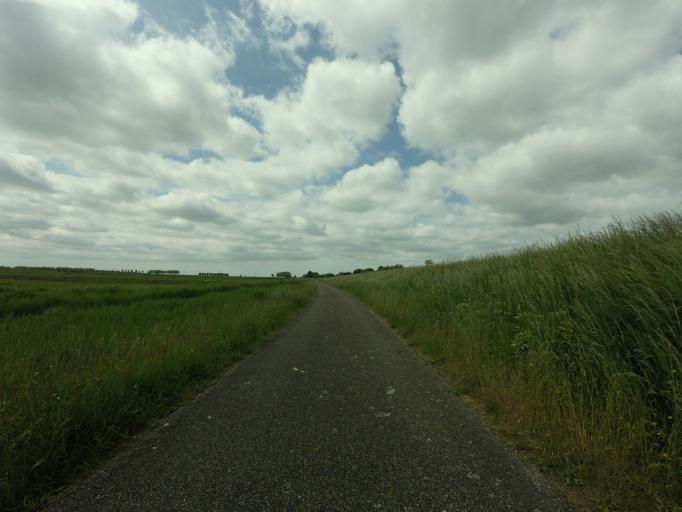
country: NL
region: North Holland
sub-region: Gemeente Hoorn
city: Hoorn
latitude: 52.6014
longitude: 5.0159
